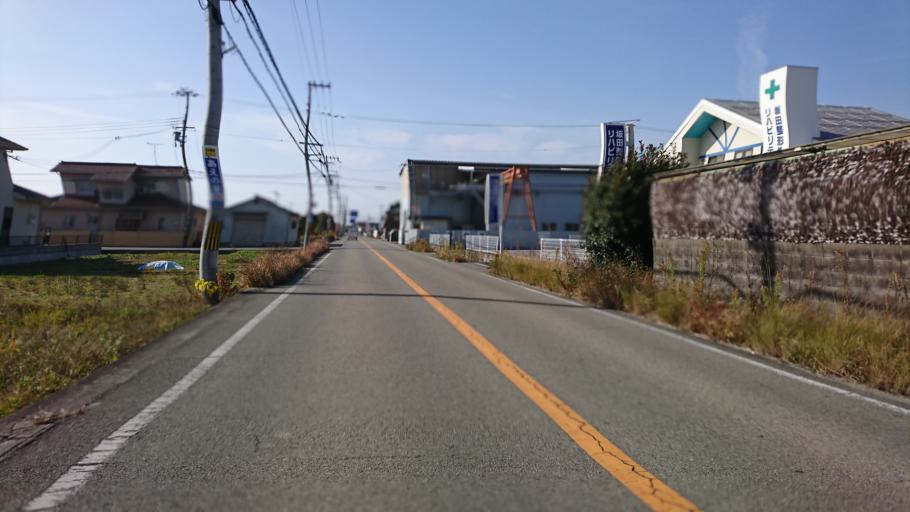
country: JP
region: Hyogo
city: Kakogawacho-honmachi
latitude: 34.7275
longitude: 134.8686
